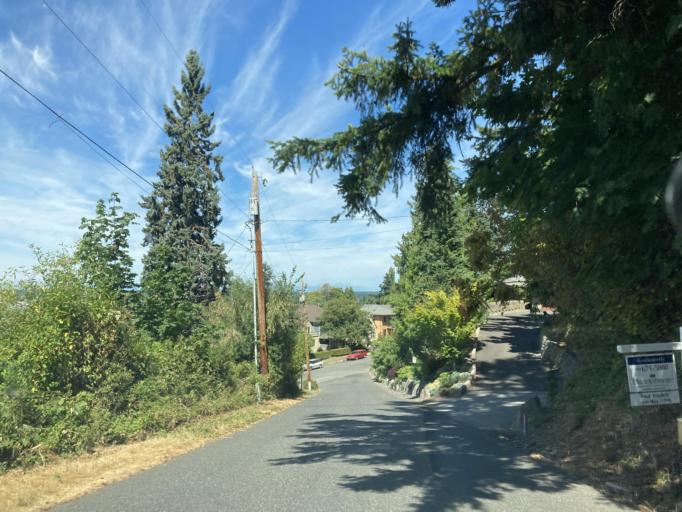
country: US
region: Washington
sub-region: Whatcom County
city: Bellingham
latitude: 48.7338
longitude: -122.4938
